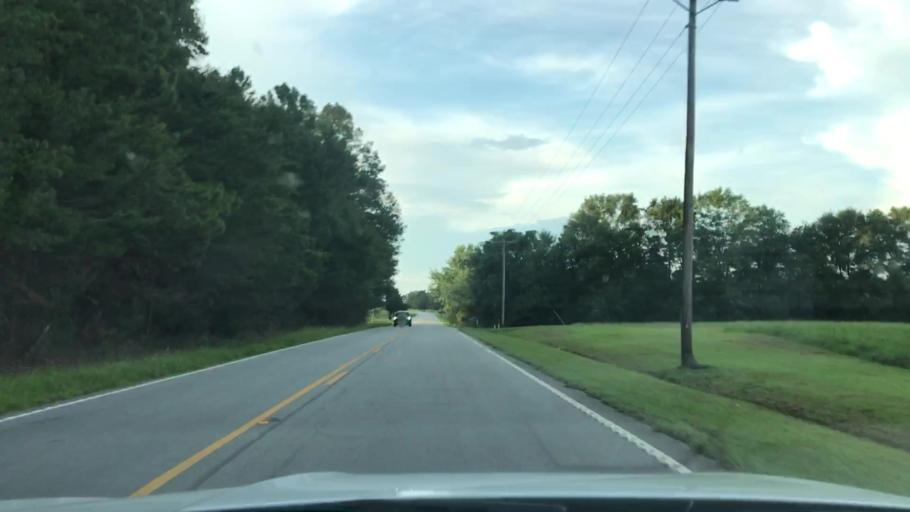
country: US
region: South Carolina
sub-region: Spartanburg County
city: Roebuck
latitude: 34.8237
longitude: -81.9239
